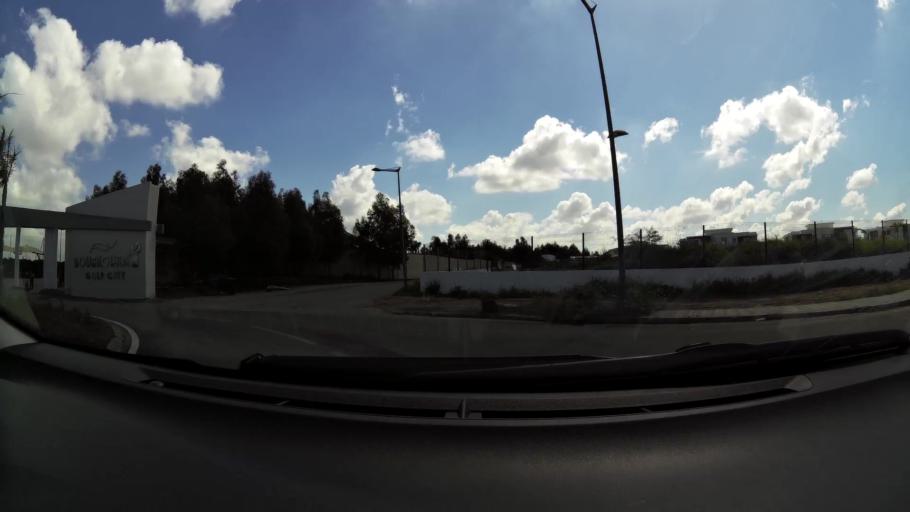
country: MA
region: Grand Casablanca
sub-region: Nouaceur
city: Bouskoura
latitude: 33.4741
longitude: -7.5998
